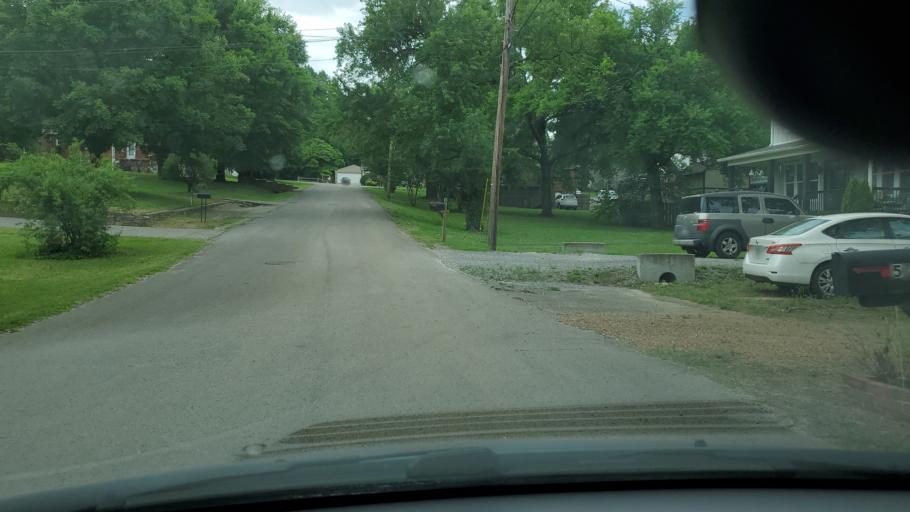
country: US
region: Tennessee
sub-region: Davidson County
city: Lakewood
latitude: 36.2332
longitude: -86.7232
